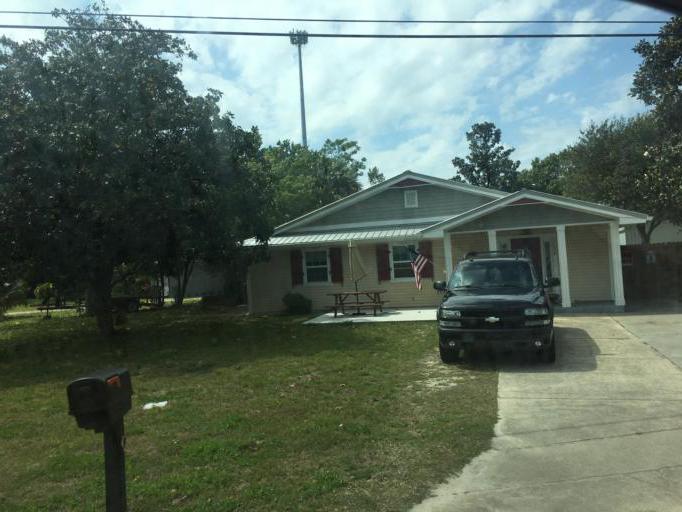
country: US
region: Florida
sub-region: Bay County
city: Laguna Beach
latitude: 30.2282
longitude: -85.8870
